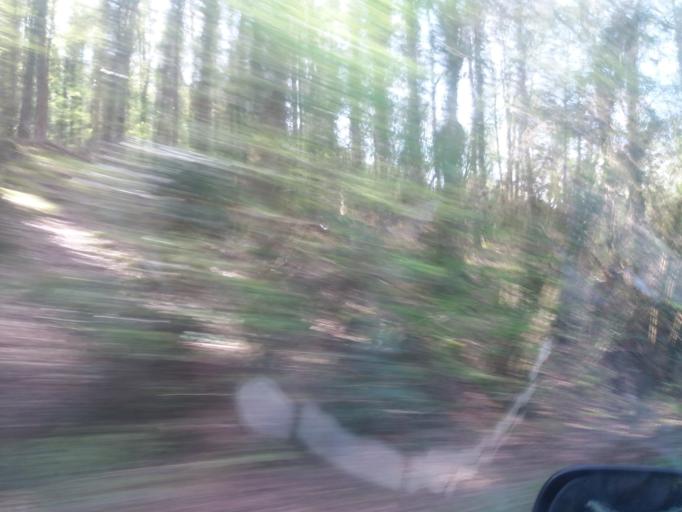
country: GB
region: Northern Ireland
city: Irvinestown
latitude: 54.4163
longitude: -7.7303
